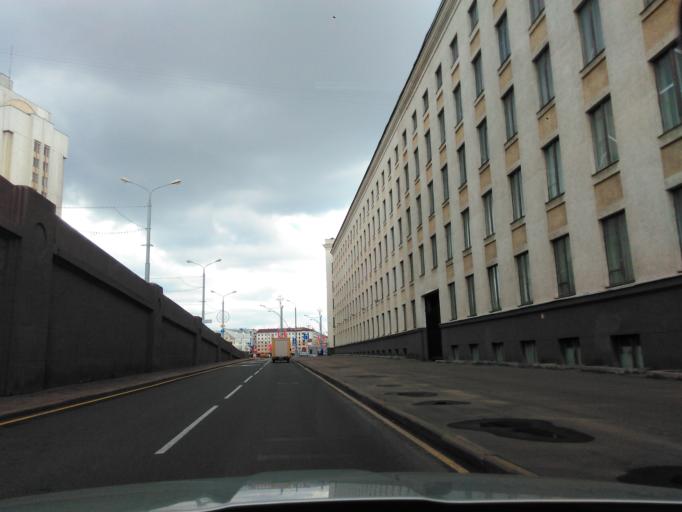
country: BY
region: Minsk
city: Minsk
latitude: 53.8930
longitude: 27.5442
